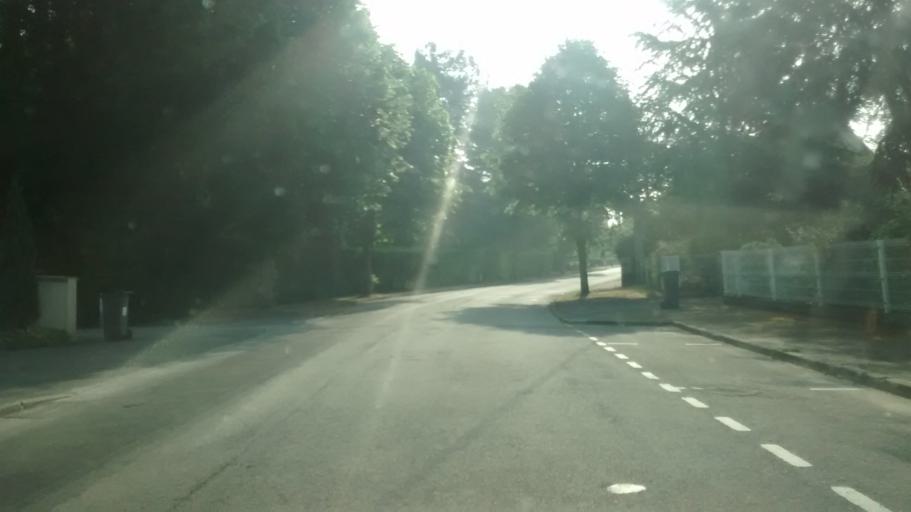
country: FR
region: Brittany
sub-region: Departement du Morbihan
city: Guer
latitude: 47.9044
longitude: -2.1294
